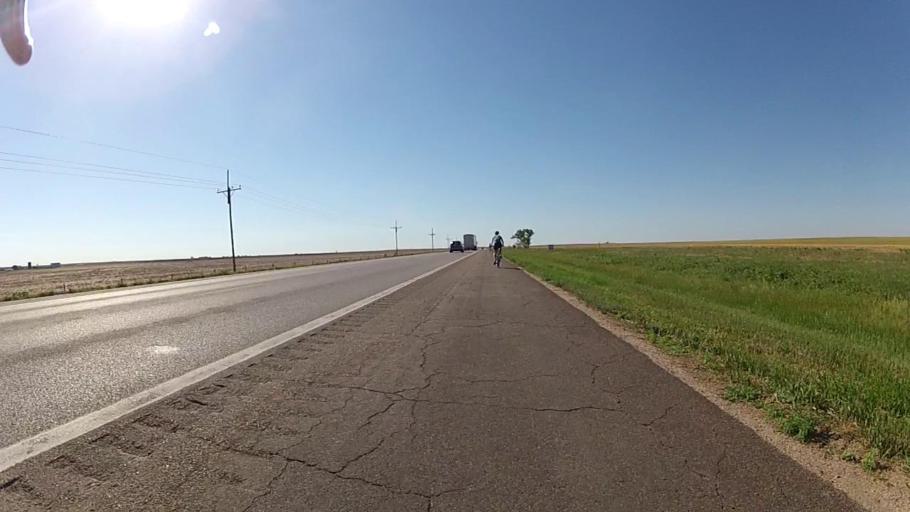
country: US
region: Kansas
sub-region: Ford County
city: Dodge City
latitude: 37.5945
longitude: -99.6937
